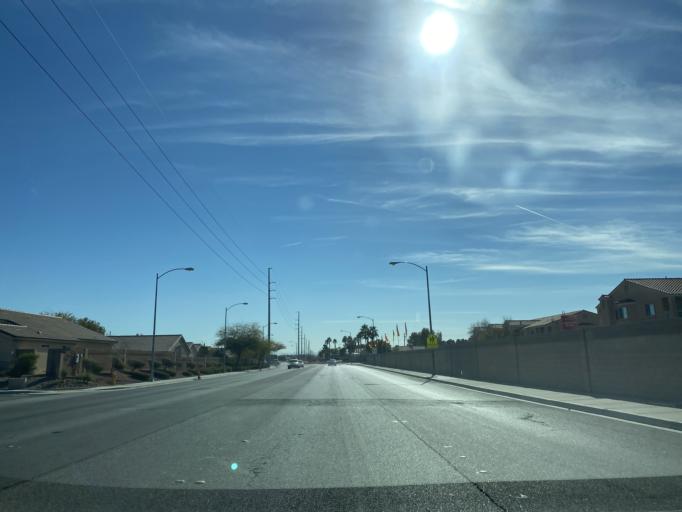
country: US
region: Nevada
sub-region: Clark County
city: North Las Vegas
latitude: 36.2495
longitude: -115.1441
